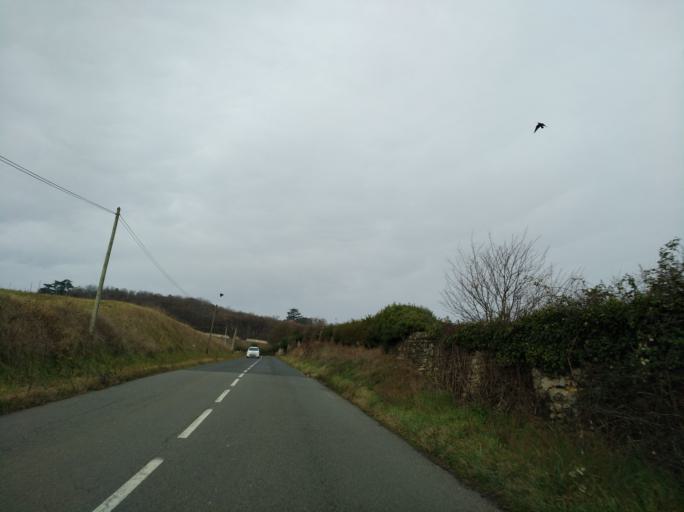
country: FR
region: Rhone-Alpes
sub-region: Departement du Rhone
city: Pommiers
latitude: 45.9505
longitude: 4.7111
